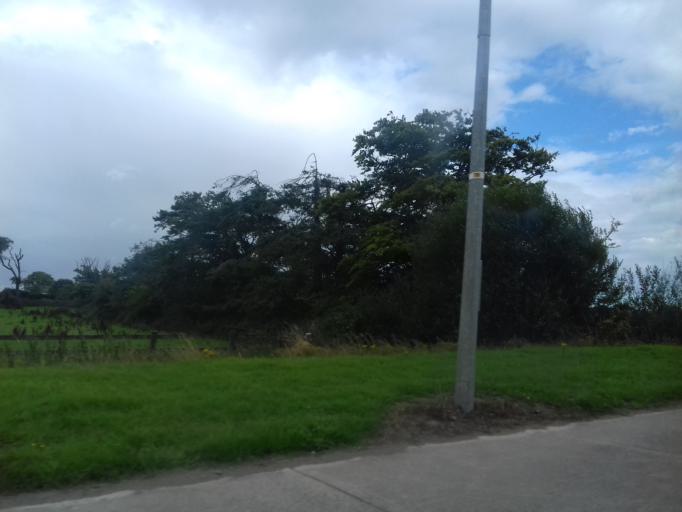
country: IE
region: Munster
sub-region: Waterford
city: Waterford
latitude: 52.2520
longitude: -7.1757
